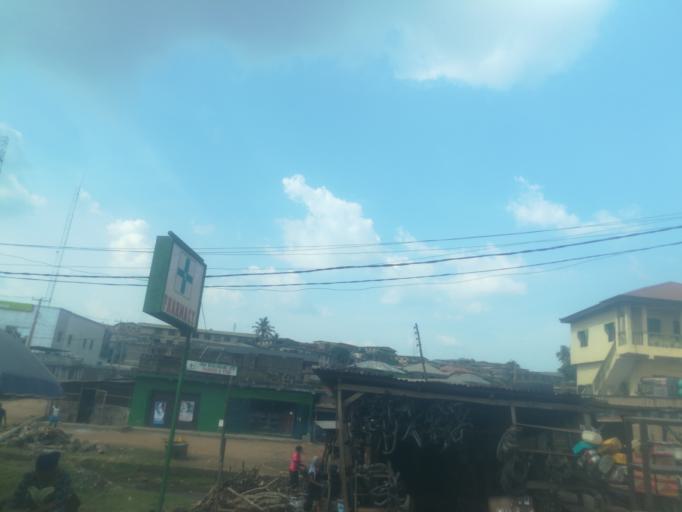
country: NG
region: Ogun
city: Abeokuta
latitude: 7.1711
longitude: 3.3663
